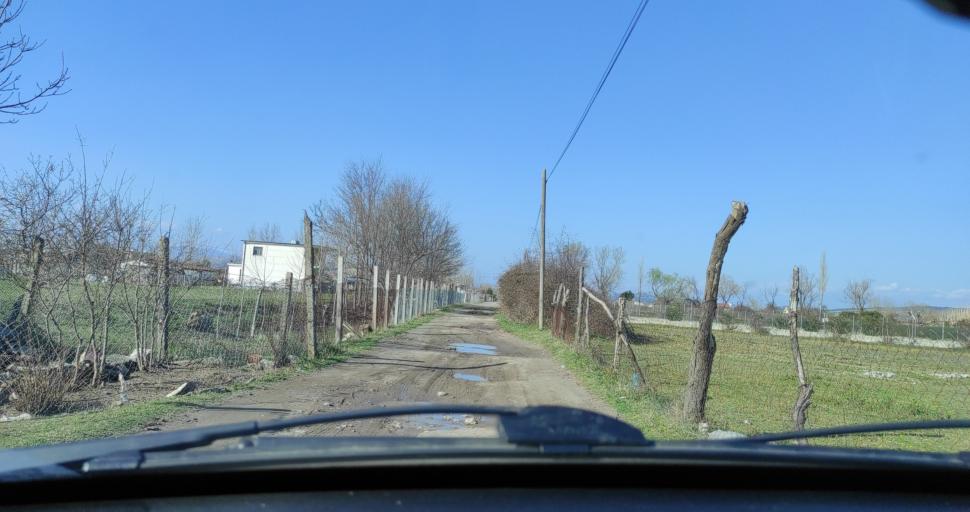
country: AL
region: Shkoder
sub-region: Rrethi i Shkodres
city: Velipoje
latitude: 41.8707
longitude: 19.4113
